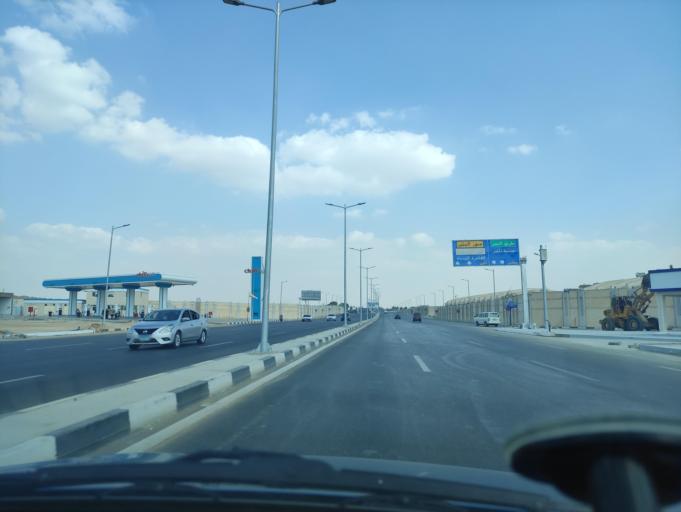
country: EG
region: Muhafazat al Qahirah
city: Cairo
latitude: 30.0421
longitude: 31.2976
